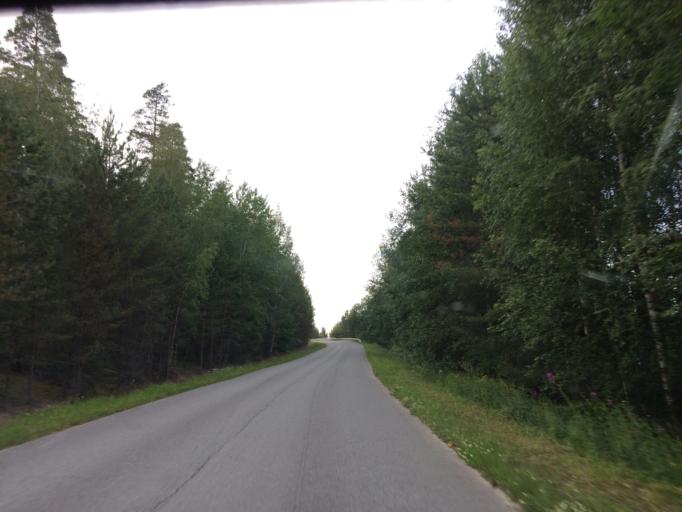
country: FI
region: Haeme
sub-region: Haemeenlinna
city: Tervakoski
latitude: 60.8420
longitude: 24.6264
